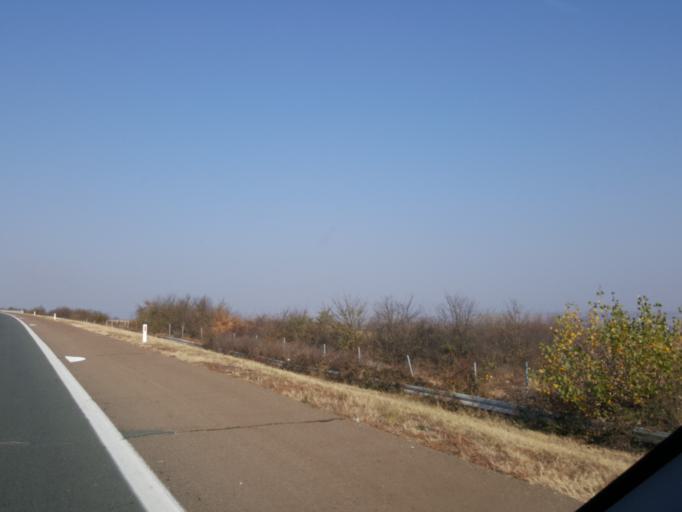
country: RS
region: Central Serbia
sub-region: Nisavski Okrug
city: Doljevac
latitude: 43.2451
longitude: 21.8172
